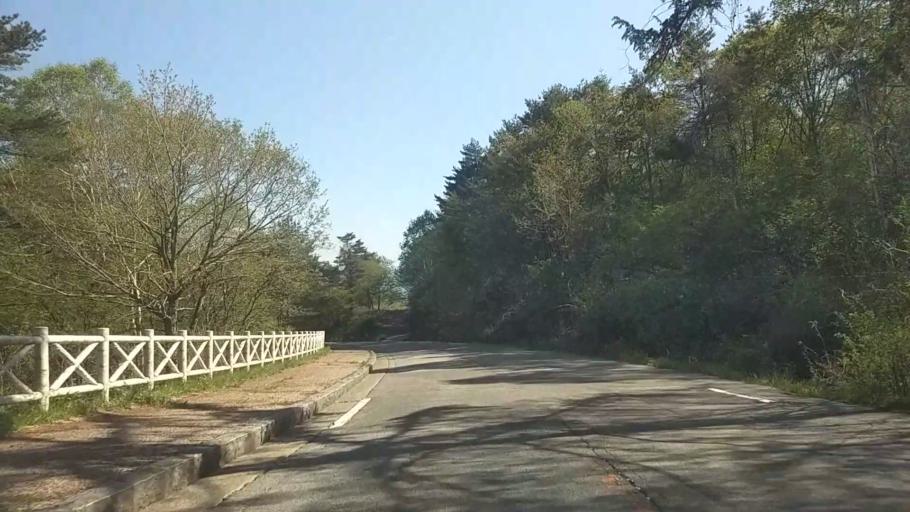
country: JP
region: Yamanashi
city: Nirasaki
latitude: 35.9277
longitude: 138.4073
